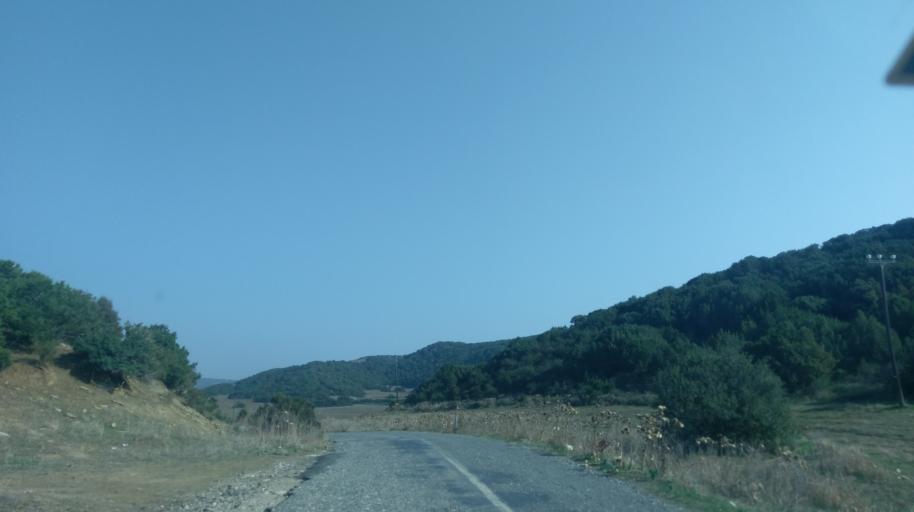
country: CY
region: Ammochostos
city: Rizokarpaso
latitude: 35.6389
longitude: 34.5161
